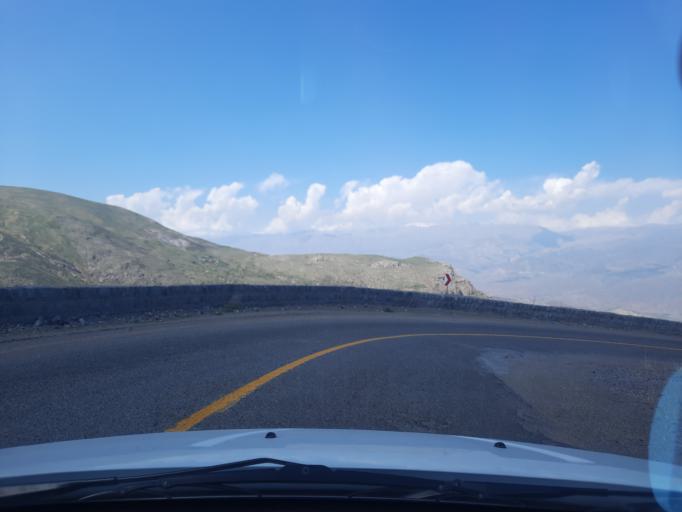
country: IR
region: Qazvin
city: Qazvin
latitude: 36.4068
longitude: 50.2210
